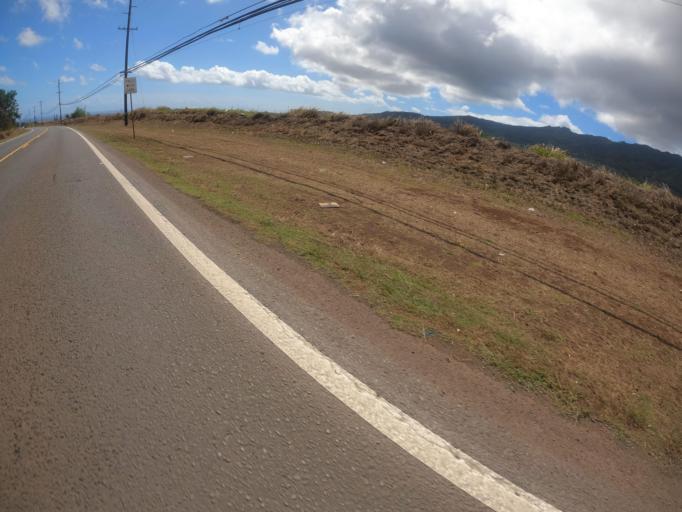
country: US
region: Hawaii
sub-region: Honolulu County
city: Village Park
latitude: 21.4272
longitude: -158.0550
